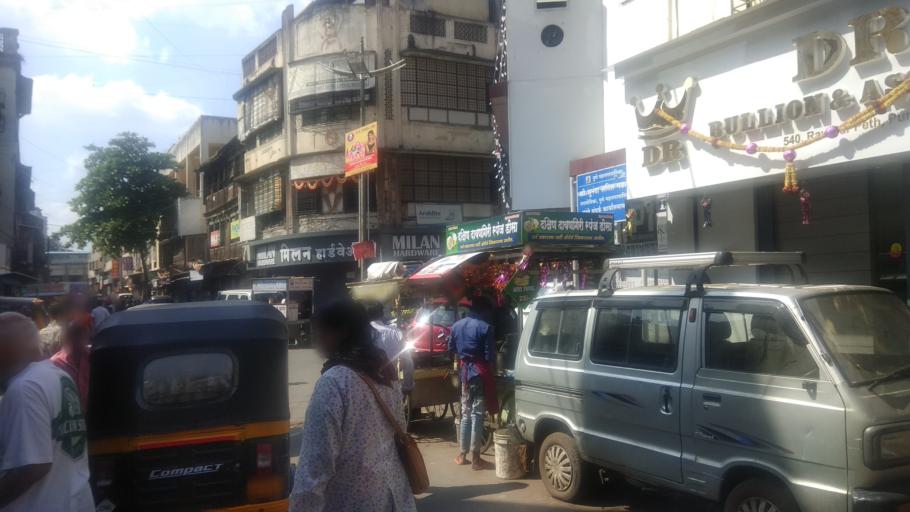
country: IN
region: Maharashtra
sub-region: Pune Division
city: Pune
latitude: 18.5156
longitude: 73.8596
